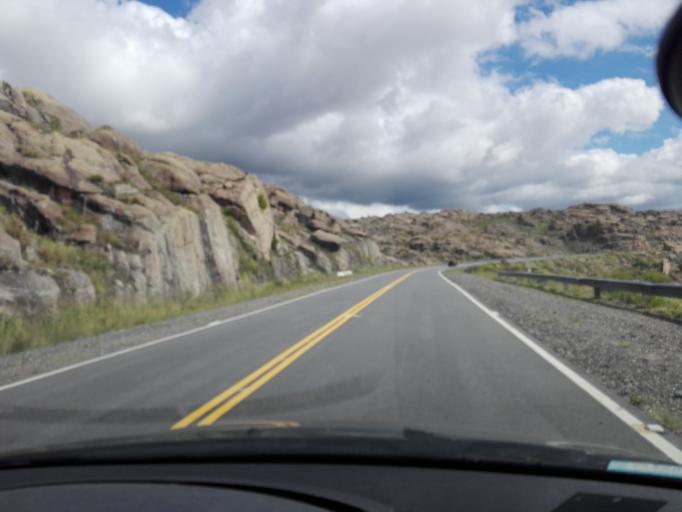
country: AR
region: Cordoba
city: Mina Clavero
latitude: -31.7519
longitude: -64.9114
